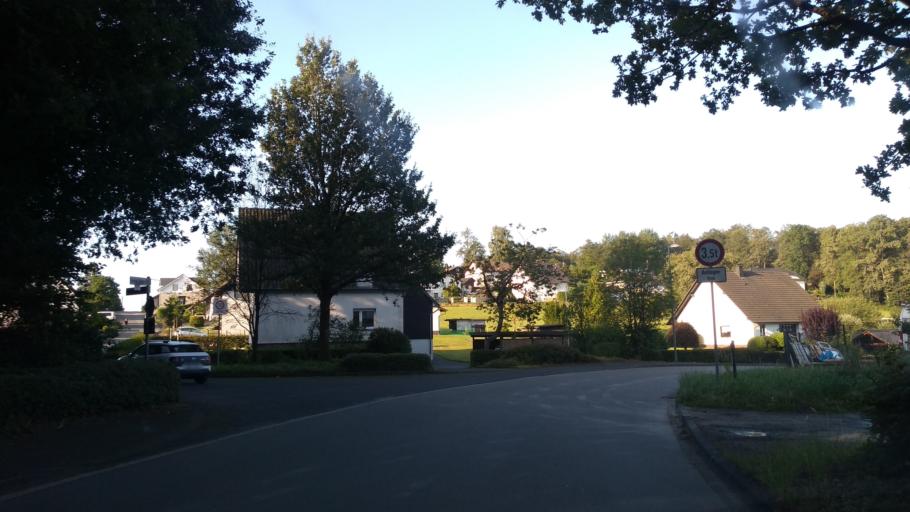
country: DE
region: North Rhine-Westphalia
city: Wiehl
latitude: 50.9708
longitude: 7.5076
